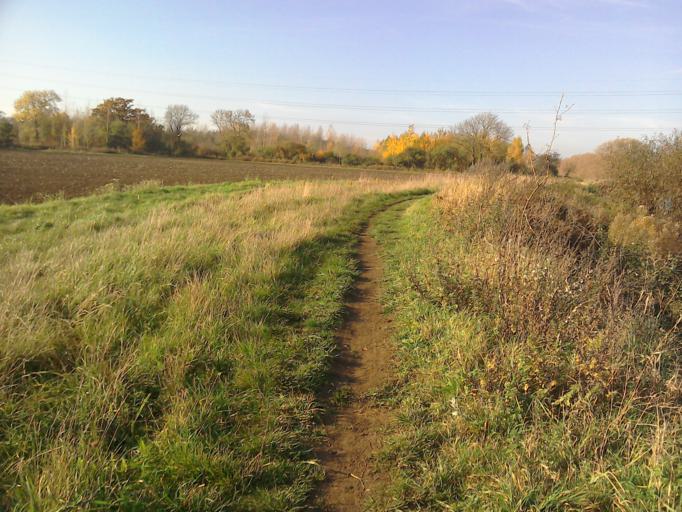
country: GB
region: England
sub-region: Oxfordshire
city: Radley
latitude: 51.6933
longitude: -1.2253
